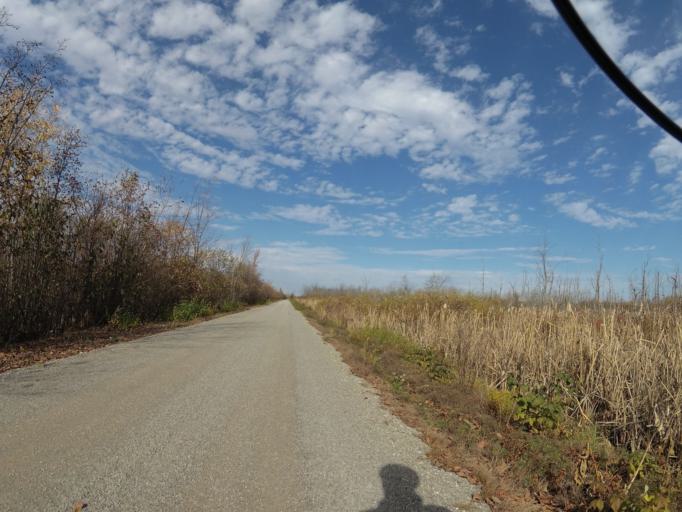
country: CA
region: Ontario
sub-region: Lanark County
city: Smiths Falls
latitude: 45.0195
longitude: -76.0746
